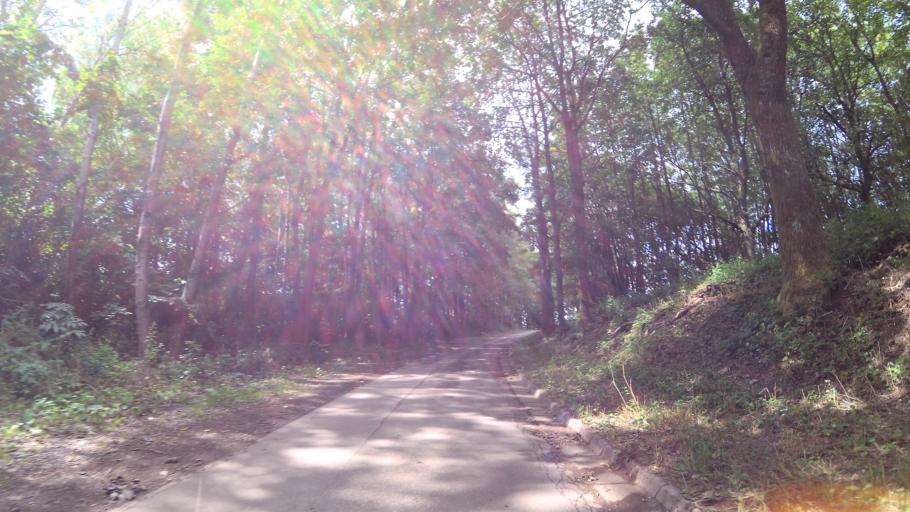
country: DE
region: Rheinland-Pfalz
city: Breitenbach
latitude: 49.4725
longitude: 7.2359
